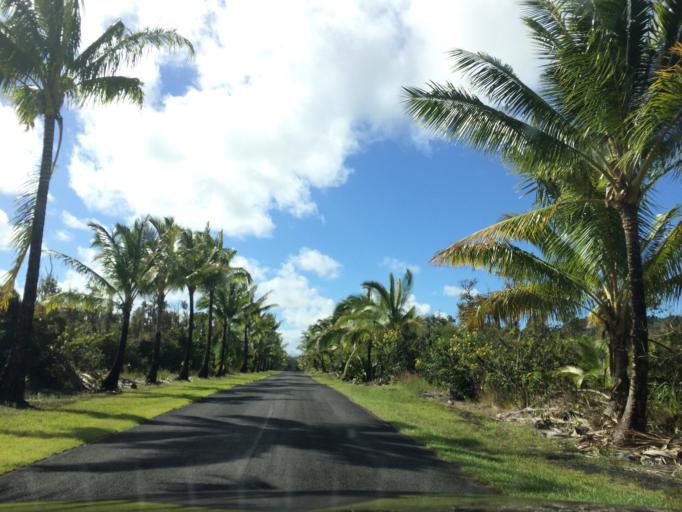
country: US
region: Hawaii
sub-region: Hawaii County
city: Nanawale Estates
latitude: 19.4918
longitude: -154.8282
